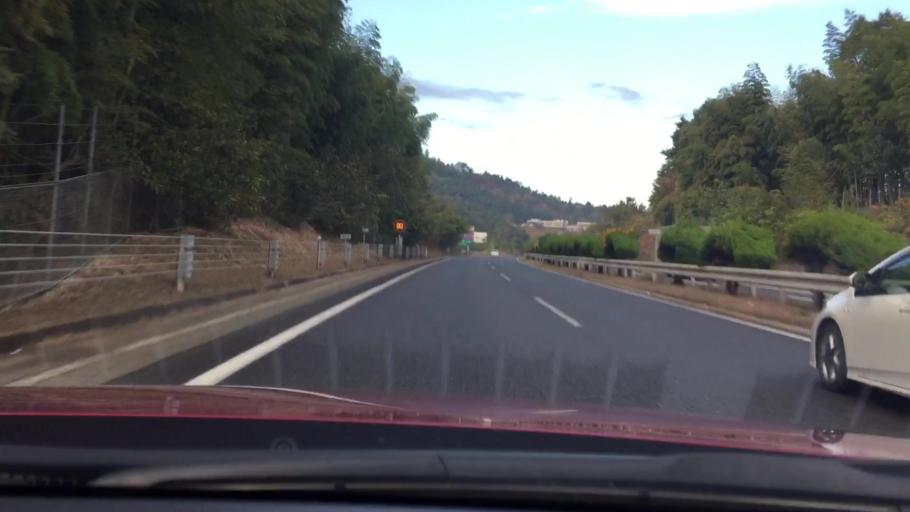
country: JP
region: Hyogo
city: Himeji
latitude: 34.9560
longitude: 134.7160
